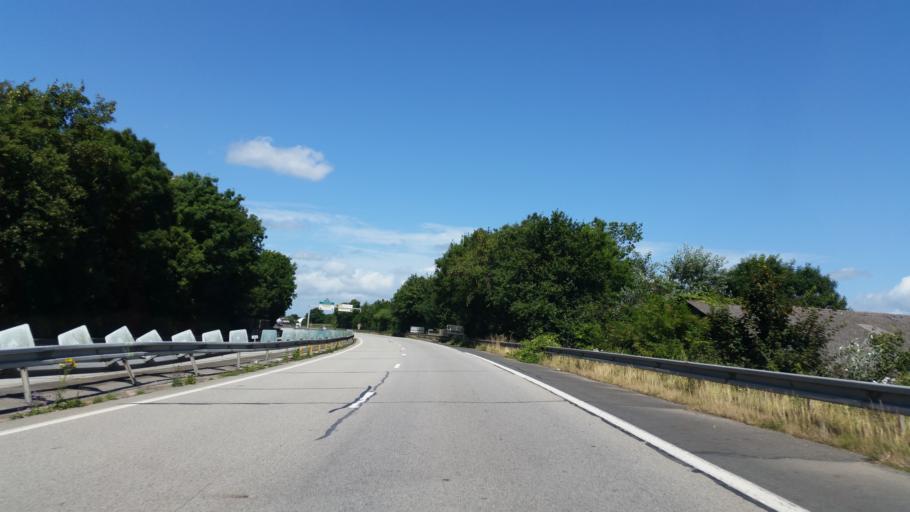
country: FR
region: Lower Normandy
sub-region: Departement de la Manche
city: Sainte-Mere-Eglise
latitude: 49.3986
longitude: -1.3072
